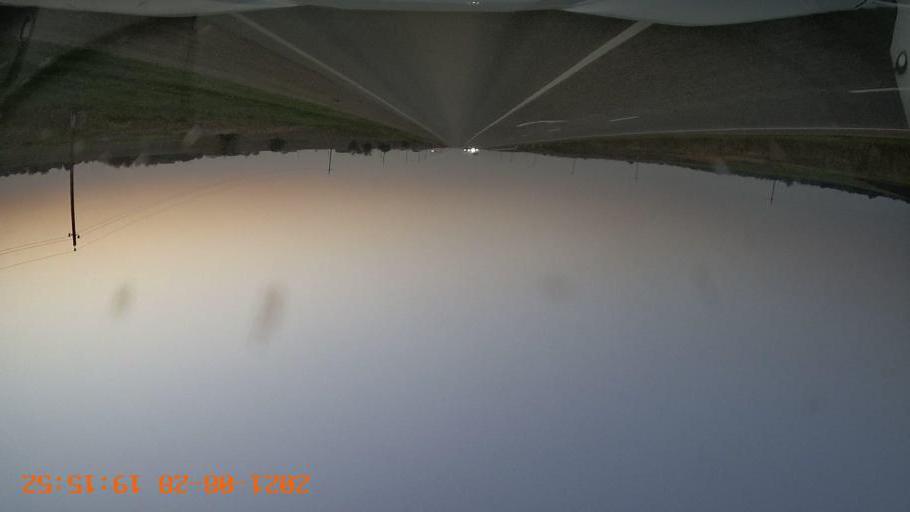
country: RU
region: Krasnodarskiy
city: Ryazanskaya
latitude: 44.9160
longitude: 39.5736
